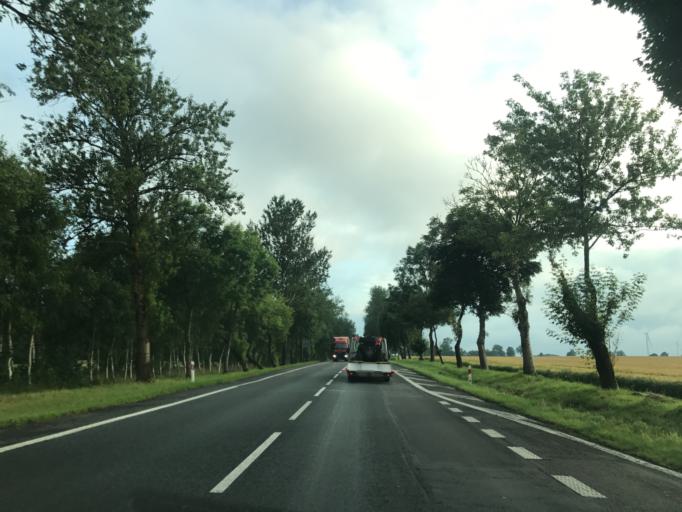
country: PL
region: West Pomeranian Voivodeship
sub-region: Powiat kolobrzeski
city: Goscino
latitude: 53.9838
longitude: 15.7084
